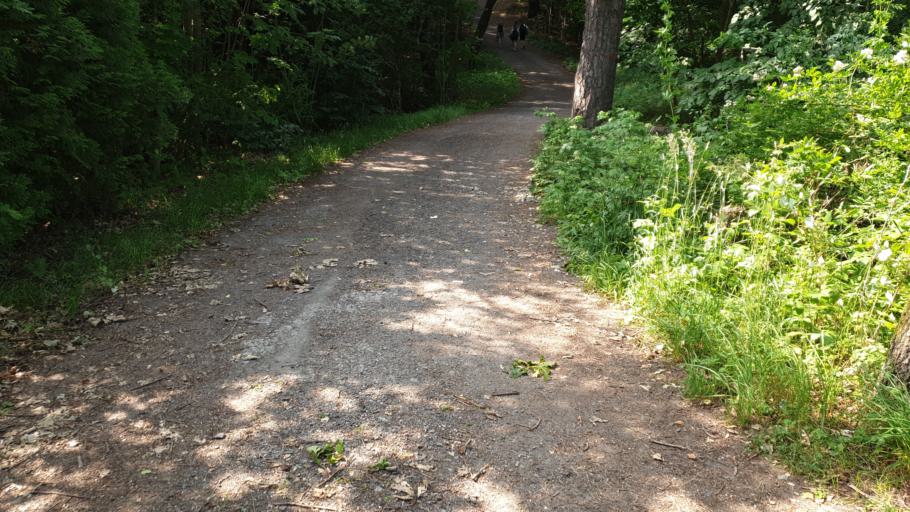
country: SE
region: Vaestra Goetaland
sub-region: Molndal
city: Moelndal
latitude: 57.6661
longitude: 12.0457
